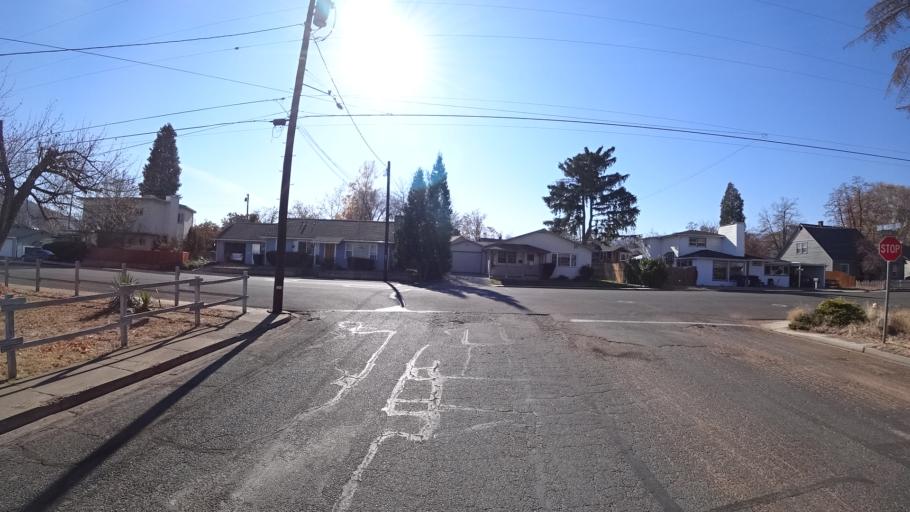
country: US
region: California
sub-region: Siskiyou County
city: Yreka
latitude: 41.7291
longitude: -122.6446
